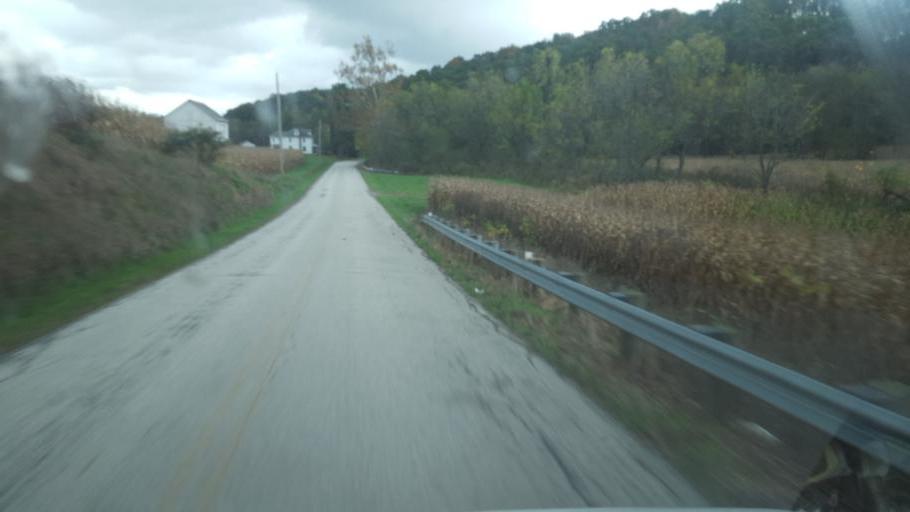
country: US
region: Ohio
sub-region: Ashland County
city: Loudonville
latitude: 40.5922
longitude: -82.1680
